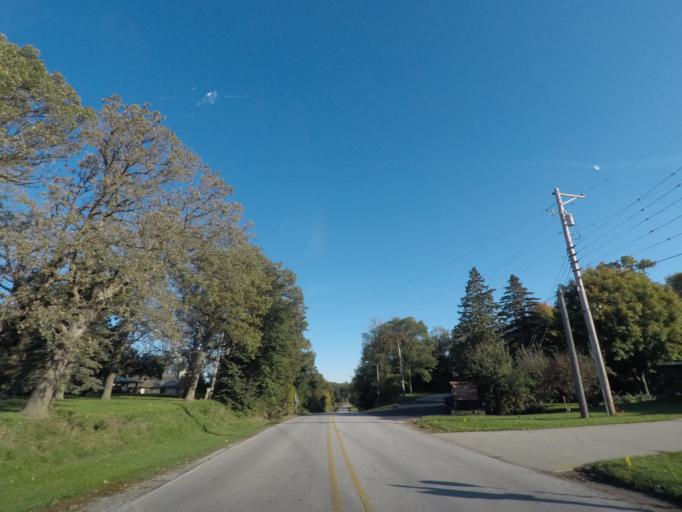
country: US
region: Iowa
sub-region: Story County
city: Nevada
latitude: 42.0160
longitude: -93.4629
